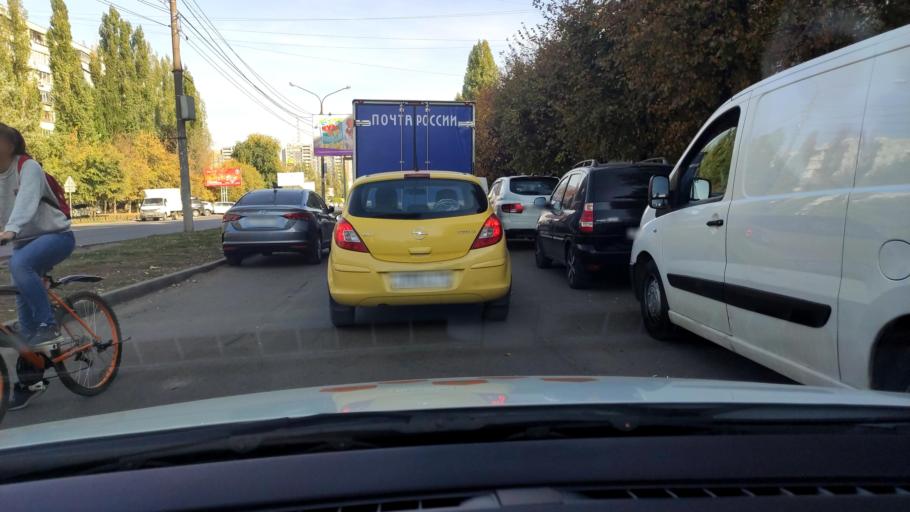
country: RU
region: Voronezj
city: Podgornoye
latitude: 51.7063
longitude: 39.1686
